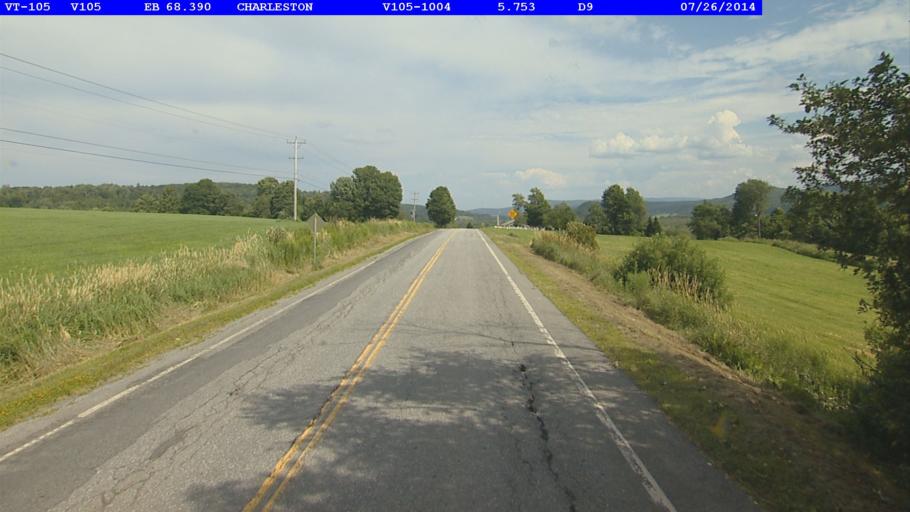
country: US
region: Vermont
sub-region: Orleans County
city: Newport
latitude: 44.8445
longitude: -72.0147
